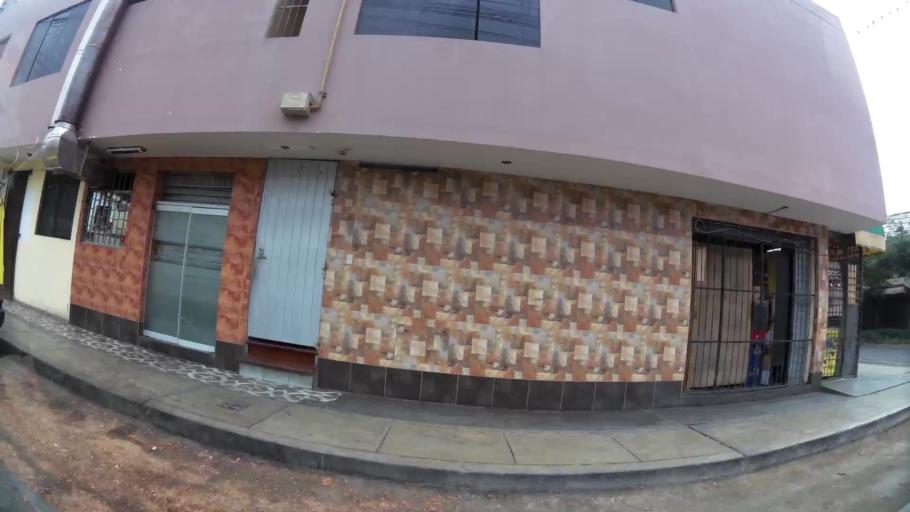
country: PE
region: Lima
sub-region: Lima
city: Surco
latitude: -12.1634
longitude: -76.9945
